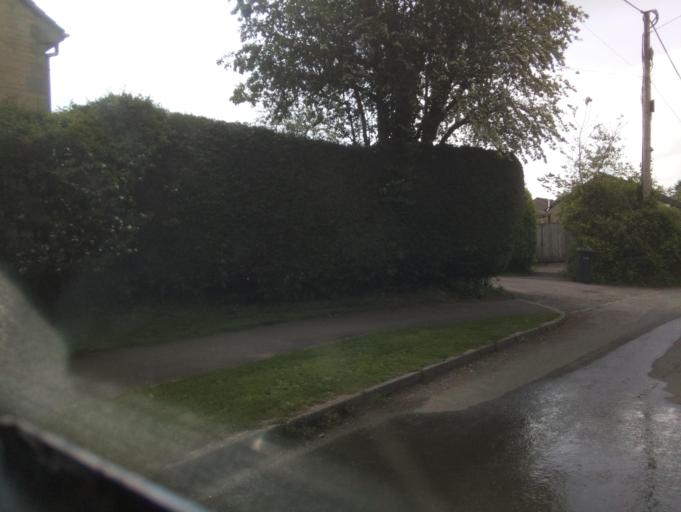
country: GB
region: England
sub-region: Wiltshire
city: Luckington
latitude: 51.5749
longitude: -2.2133
